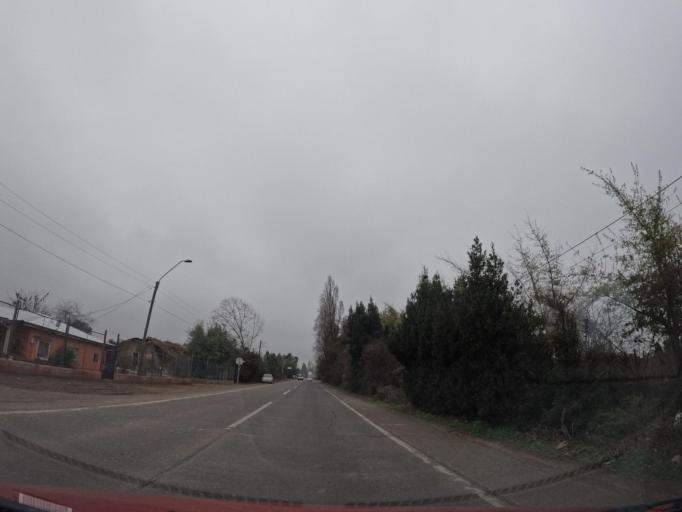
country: CL
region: Maule
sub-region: Provincia de Talca
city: San Clemente
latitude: -35.5663
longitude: -71.4459
